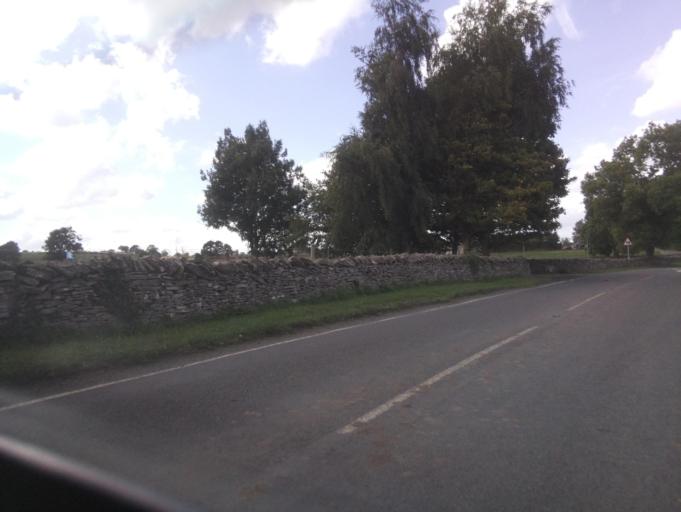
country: GB
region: England
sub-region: North Yorkshire
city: Leyburn
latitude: 54.2809
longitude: -1.7833
